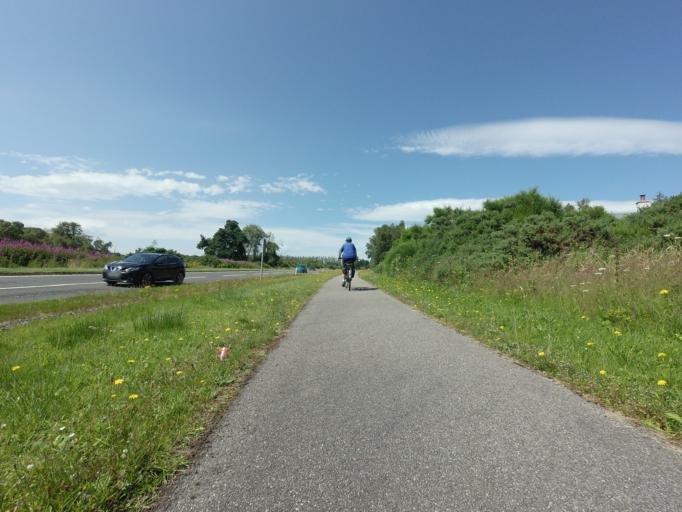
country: GB
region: Scotland
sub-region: Highland
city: Conon Bridge
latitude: 57.5389
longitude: -4.3687
